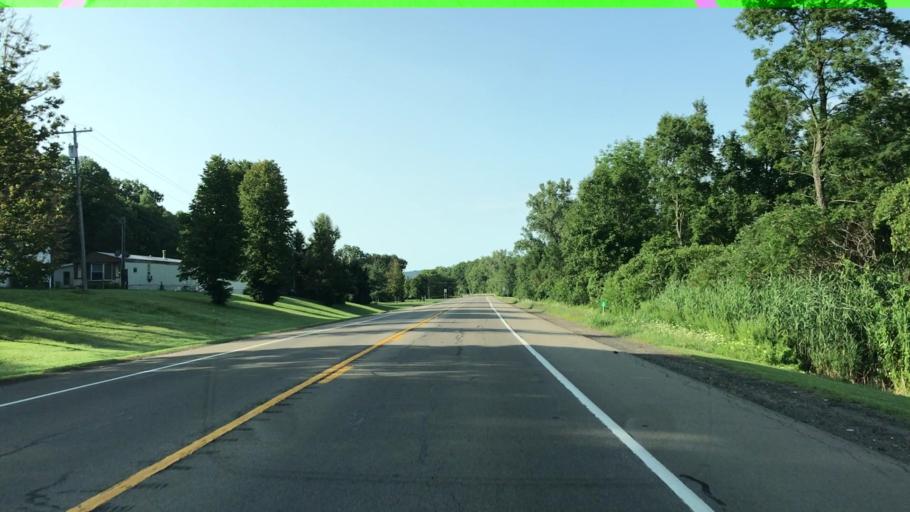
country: US
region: New York
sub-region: Chautauqua County
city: Fredonia
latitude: 42.3583
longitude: -79.3113
